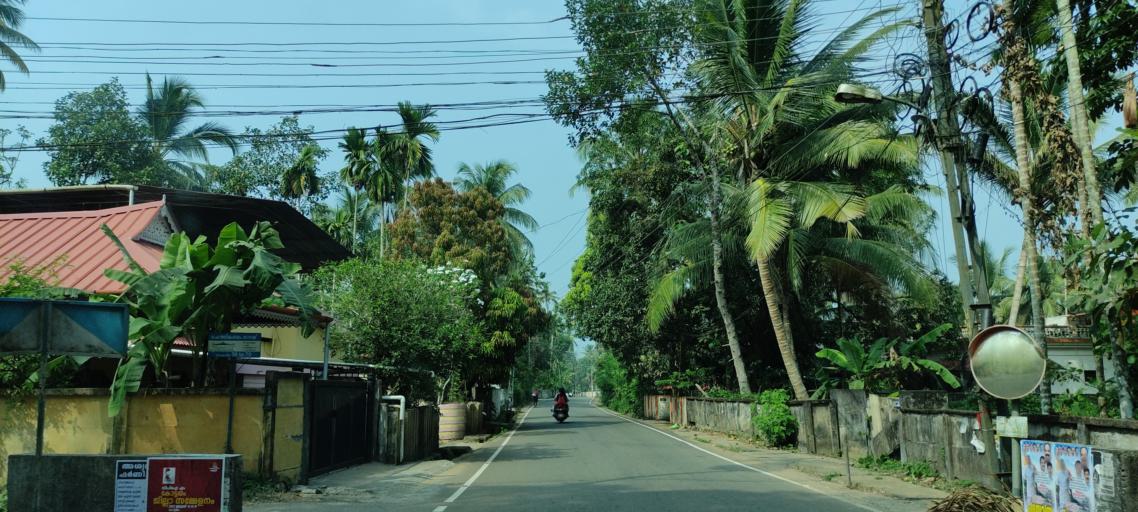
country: IN
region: Kerala
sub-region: Kottayam
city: Vaikam
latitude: 9.7539
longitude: 76.4023
